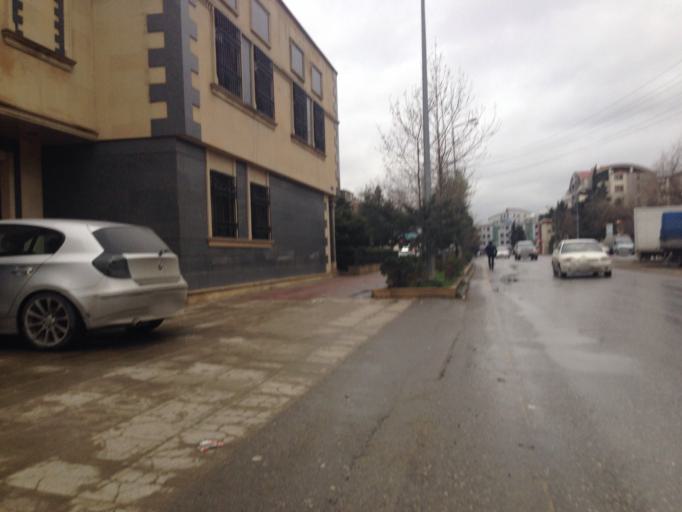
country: AZ
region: Baki
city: Baku
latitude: 40.4100
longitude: 49.8672
